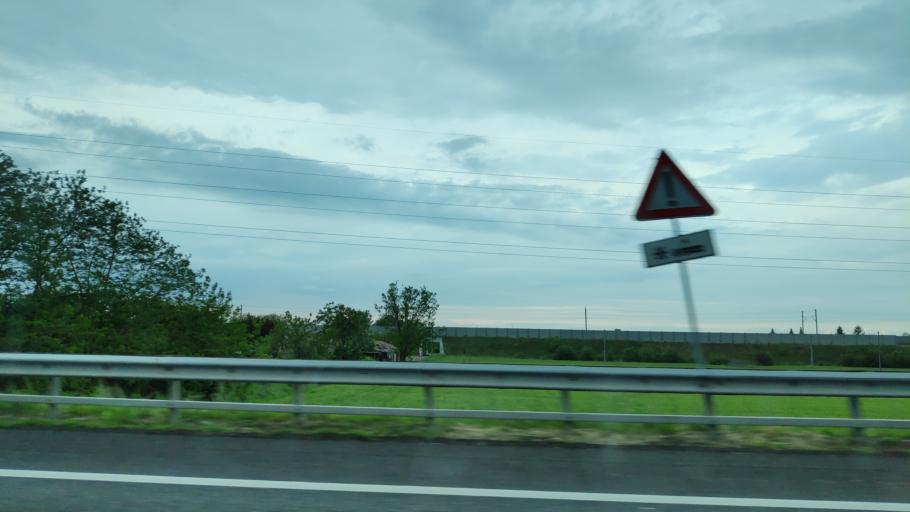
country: IT
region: Emilia-Romagna
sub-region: Provincia di Parma
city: Ponte Taro
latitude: 44.8614
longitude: 10.2493
